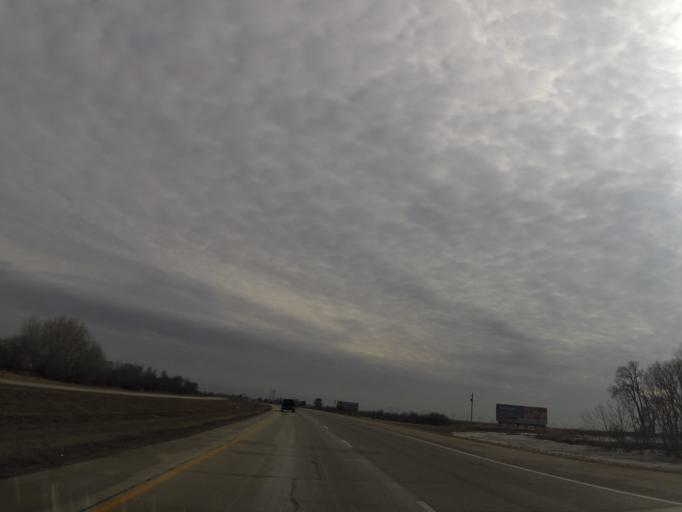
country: US
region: North Dakota
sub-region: Grand Forks County
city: Grand Forks
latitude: 47.9780
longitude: -97.0957
